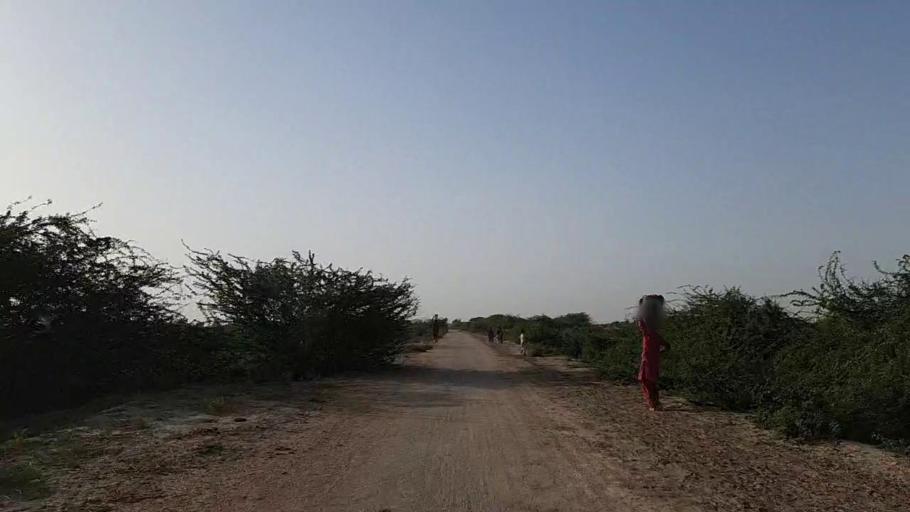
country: PK
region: Sindh
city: Jati
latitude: 24.3315
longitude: 68.1578
